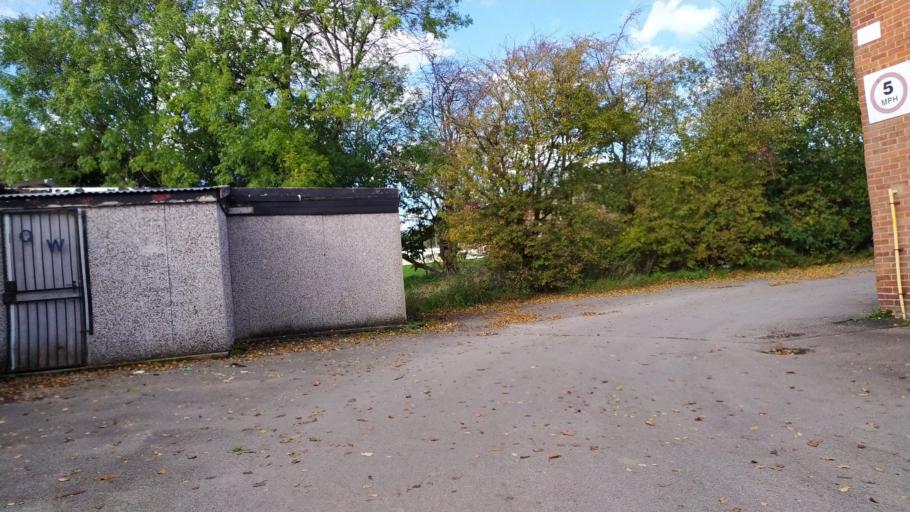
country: GB
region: England
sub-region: City and Borough of Leeds
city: Horsforth
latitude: 53.8204
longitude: -1.5960
